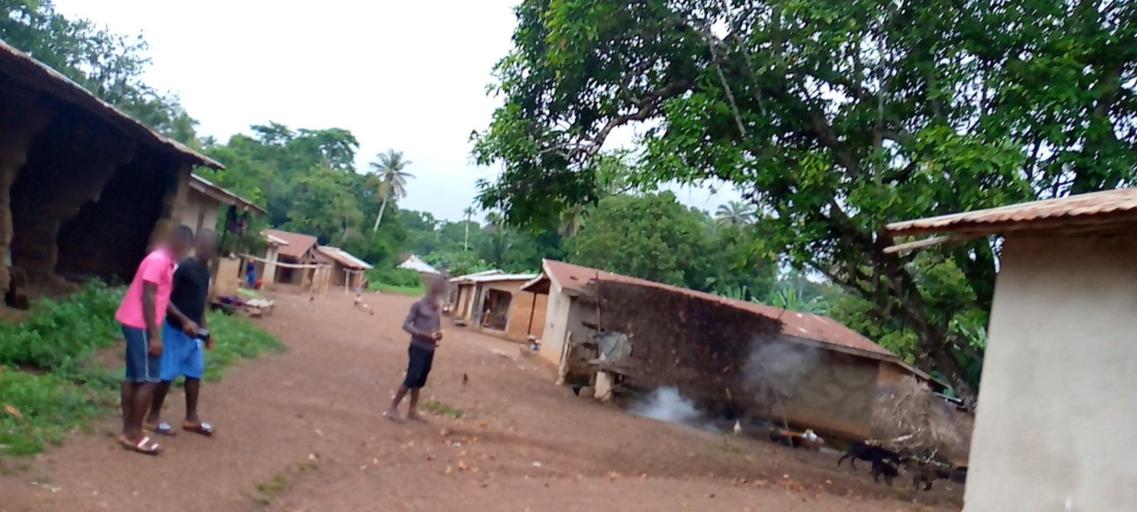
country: SL
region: Northern Province
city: Port Loko
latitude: 8.7134
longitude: -12.8050
